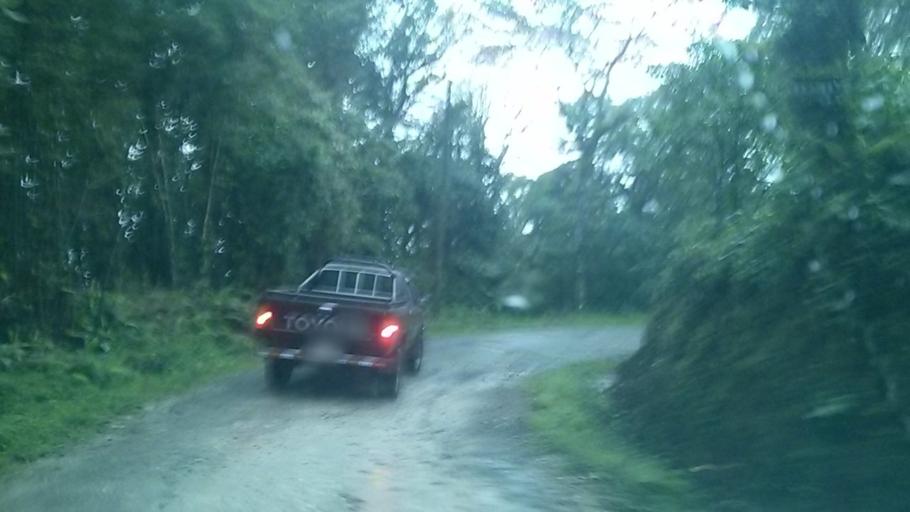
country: CR
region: San Jose
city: Ipis
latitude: 10.0251
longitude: -83.9453
